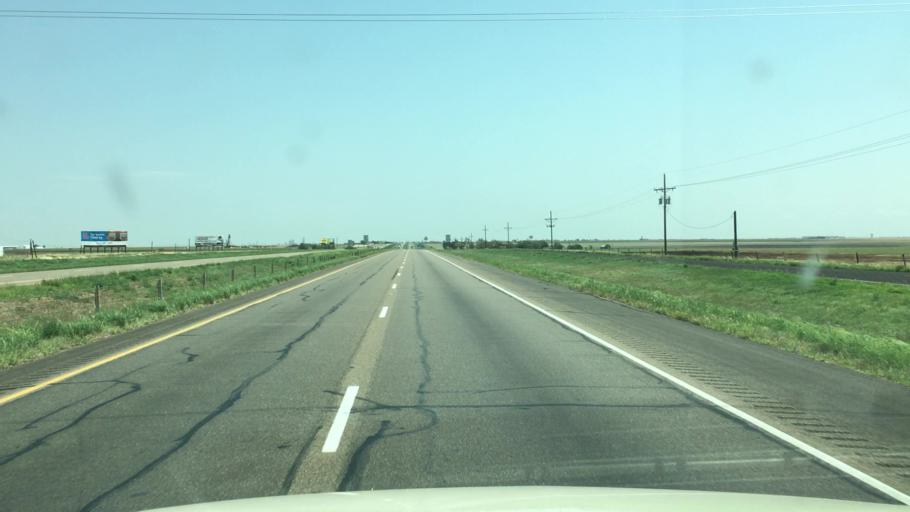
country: US
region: Texas
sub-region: Potter County
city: Bushland
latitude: 35.1908
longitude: -102.0463
